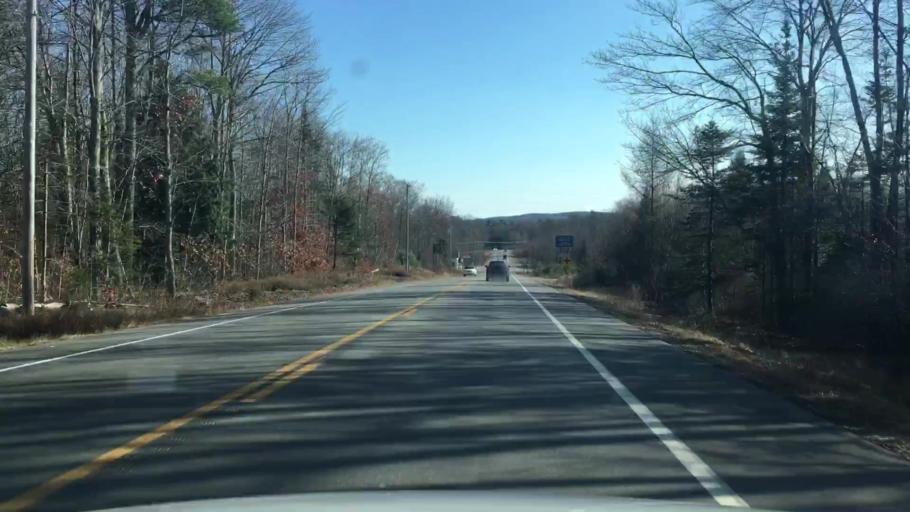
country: US
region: Maine
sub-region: Knox County
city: Washington
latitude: 44.2451
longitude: -69.3850
